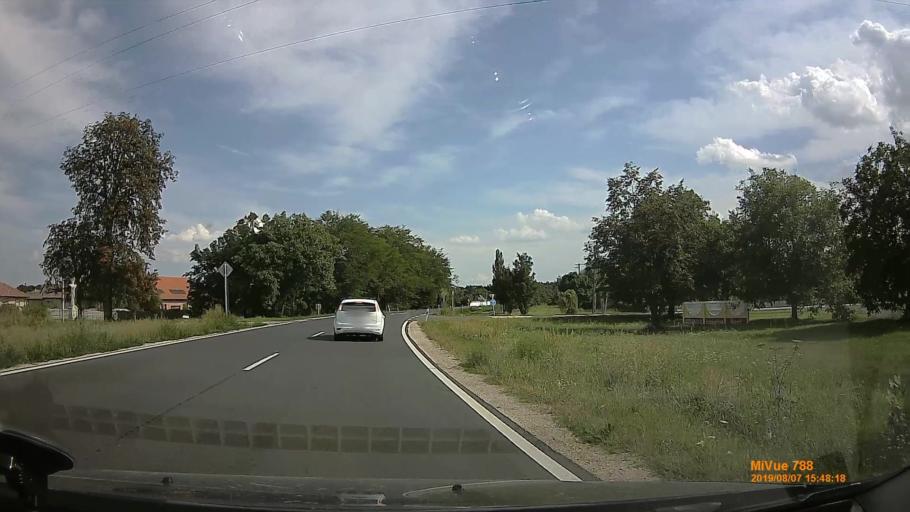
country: HU
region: Vas
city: Jak
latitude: 47.1623
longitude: 16.6365
